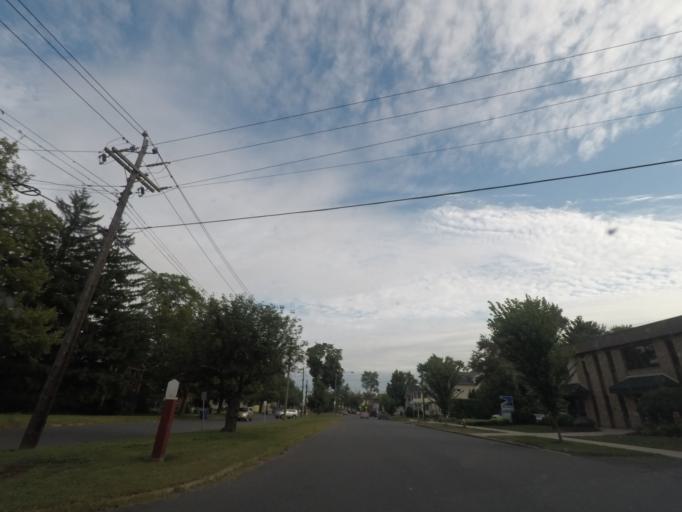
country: US
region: Massachusetts
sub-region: Hampden County
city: West Springfield
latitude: 42.1096
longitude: -72.6246
